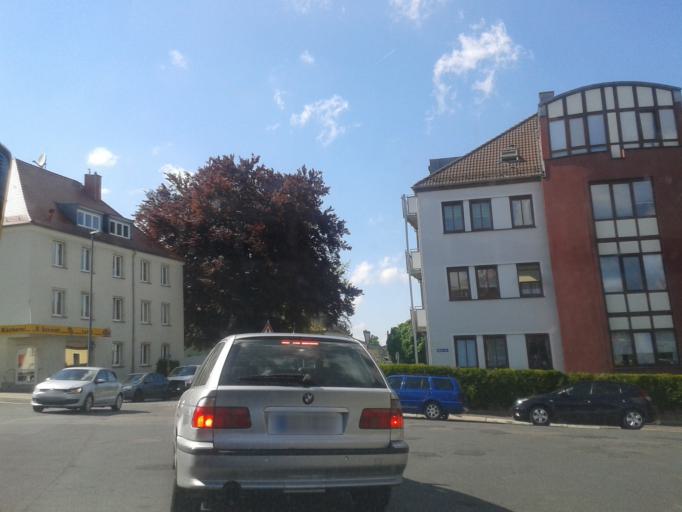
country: DE
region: Saxony
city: Freital
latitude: 51.0347
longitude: 13.6870
